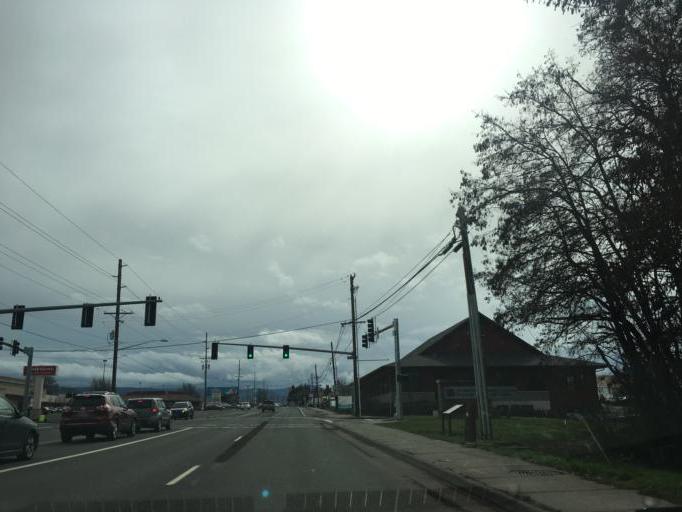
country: US
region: Oregon
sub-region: Hood River County
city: Hood River
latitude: 45.6971
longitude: -121.5237
